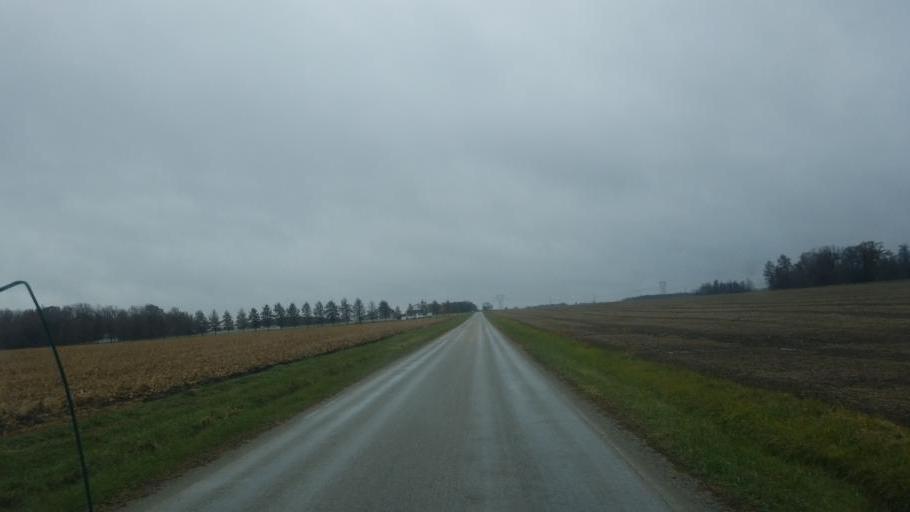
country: US
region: Indiana
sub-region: Adams County
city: Berne
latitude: 40.6944
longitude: -84.9173
